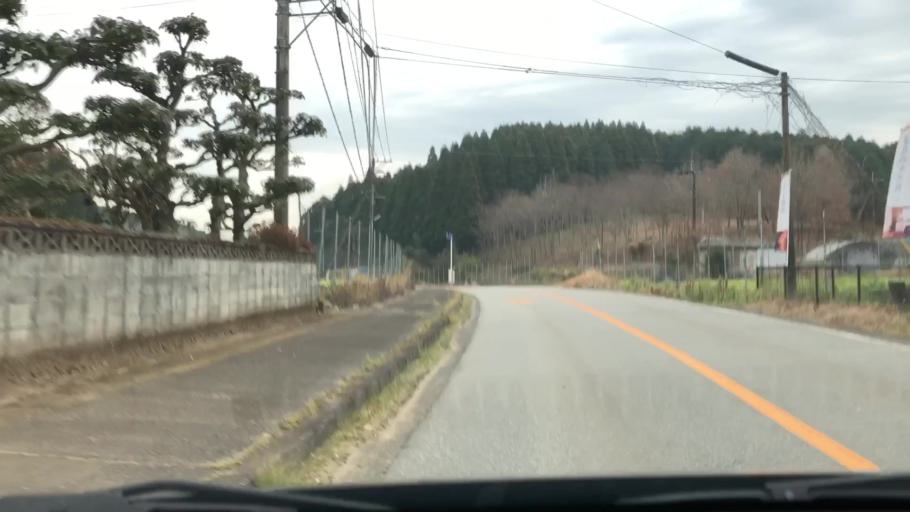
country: JP
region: Oita
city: Usuki
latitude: 33.0047
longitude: 131.6550
